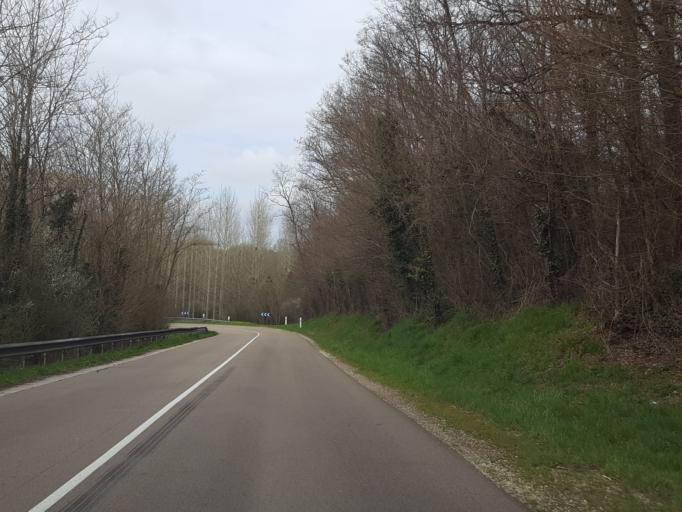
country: FR
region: Centre
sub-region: Departement du Loiret
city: Sainte-Genevieve-des-Bois
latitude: 47.8239
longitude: 2.8191
